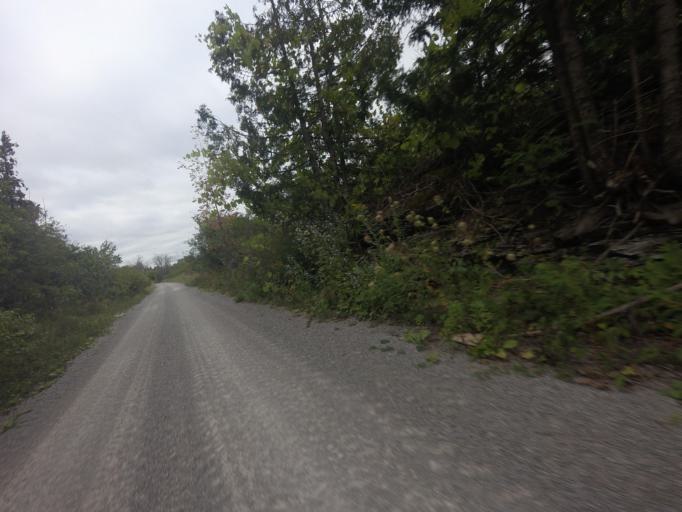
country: CA
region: Ontario
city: Omemee
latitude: 44.5228
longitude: -78.7330
